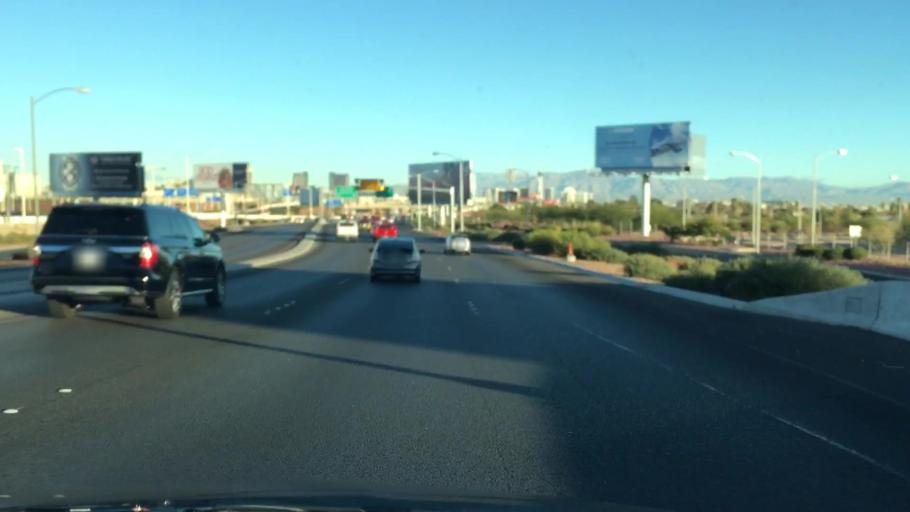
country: US
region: Nevada
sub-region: Clark County
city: Paradise
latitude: 36.0863
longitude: -115.1450
